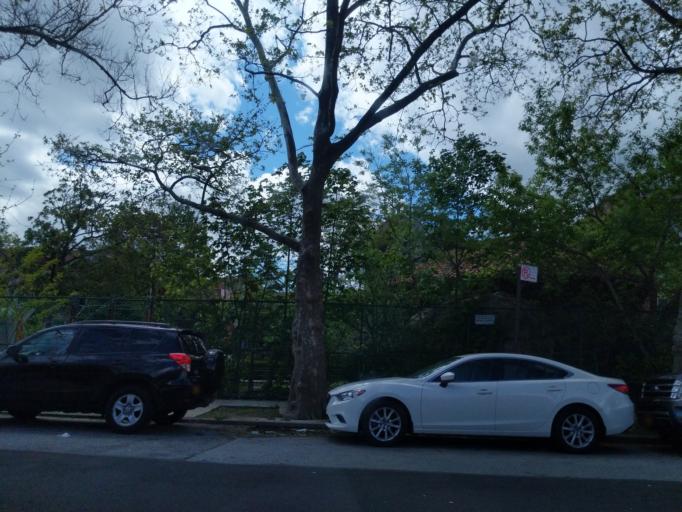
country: US
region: New York
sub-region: Bronx
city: The Bronx
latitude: 40.8638
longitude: -73.8617
